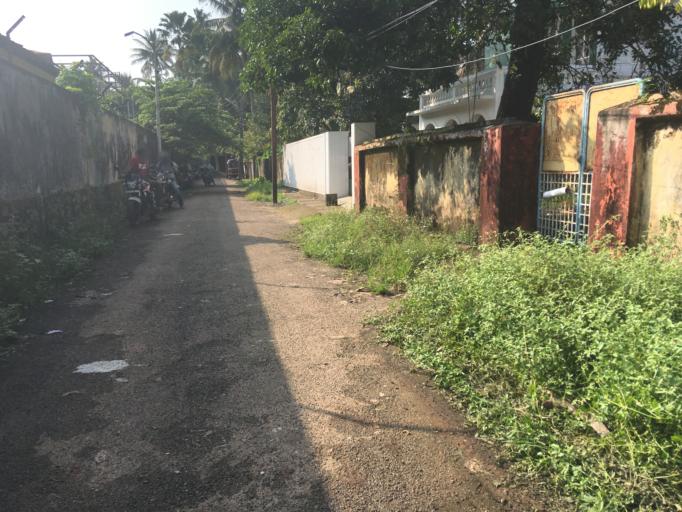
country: IN
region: Kerala
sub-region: Ernakulam
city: Cochin
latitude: 9.9615
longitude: 76.2395
